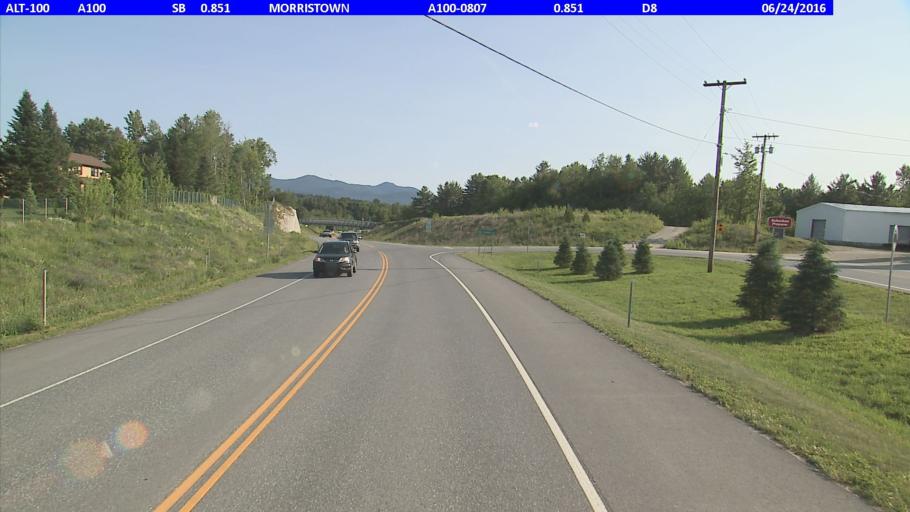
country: US
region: Vermont
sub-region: Lamoille County
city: Morrisville
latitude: 44.5683
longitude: -72.6035
